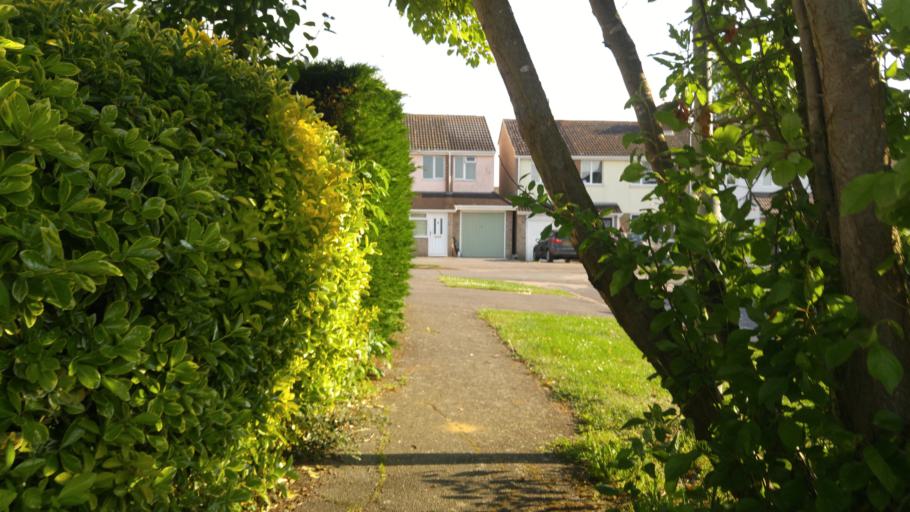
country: GB
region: England
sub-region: Essex
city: Eight Ash Green
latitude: 51.9194
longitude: 0.8003
